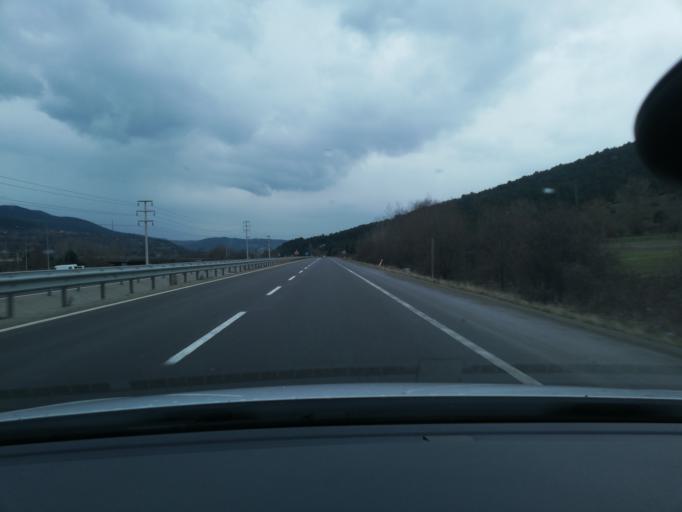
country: TR
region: Bolu
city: Yenicaga
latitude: 40.7451
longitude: 31.8604
